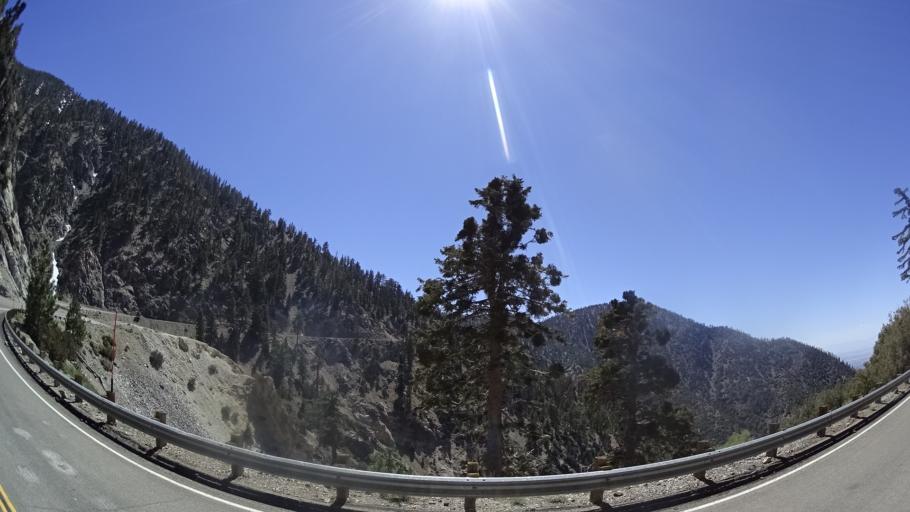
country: US
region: California
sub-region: San Bernardino County
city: Wrightwood
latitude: 34.3694
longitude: -117.7806
